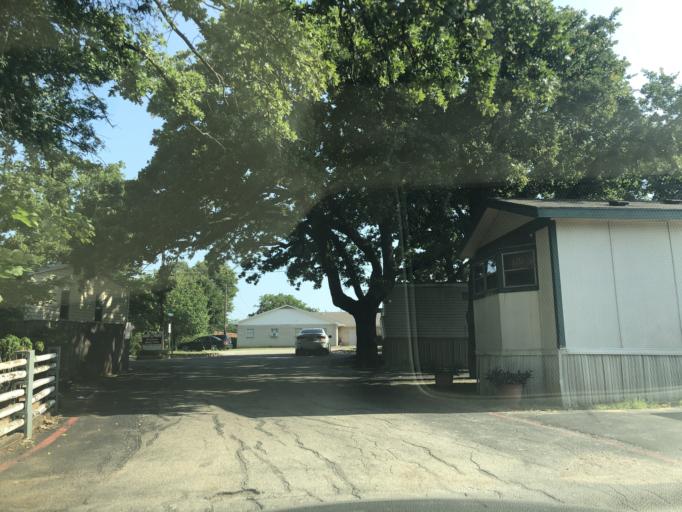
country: US
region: Texas
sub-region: Dallas County
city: Irving
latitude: 32.8066
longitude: -96.9907
